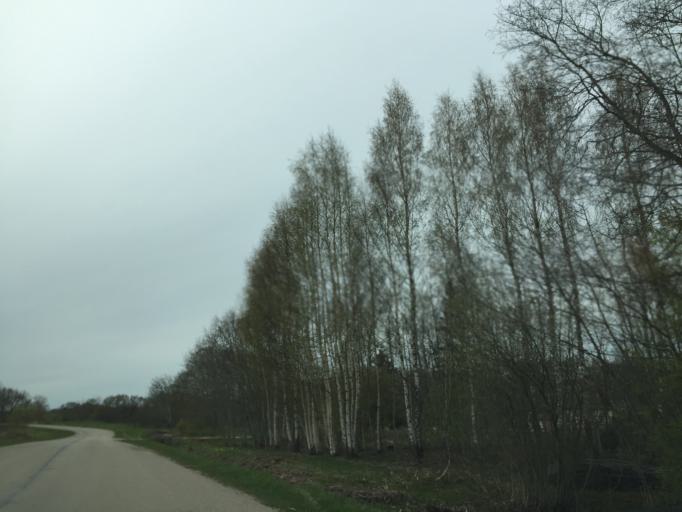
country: LV
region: Ludzas Rajons
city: Ludza
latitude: 56.5676
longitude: 27.7434
